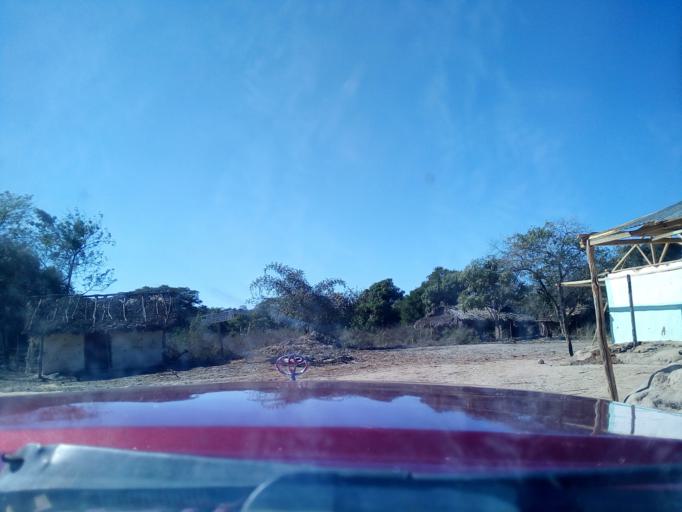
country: MG
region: Boeny
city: Sitampiky
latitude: -16.2163
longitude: 45.3627
